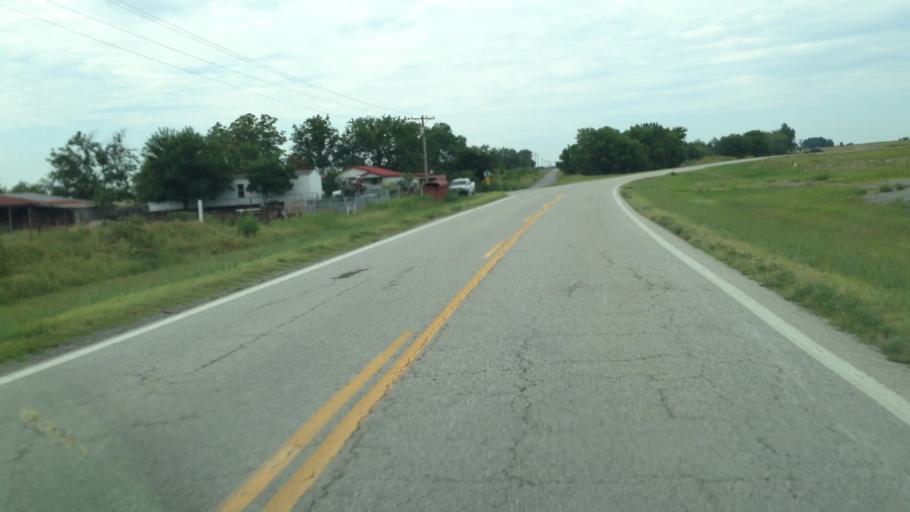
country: US
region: Oklahoma
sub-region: Craig County
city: Vinita
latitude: 36.8184
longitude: -95.1436
